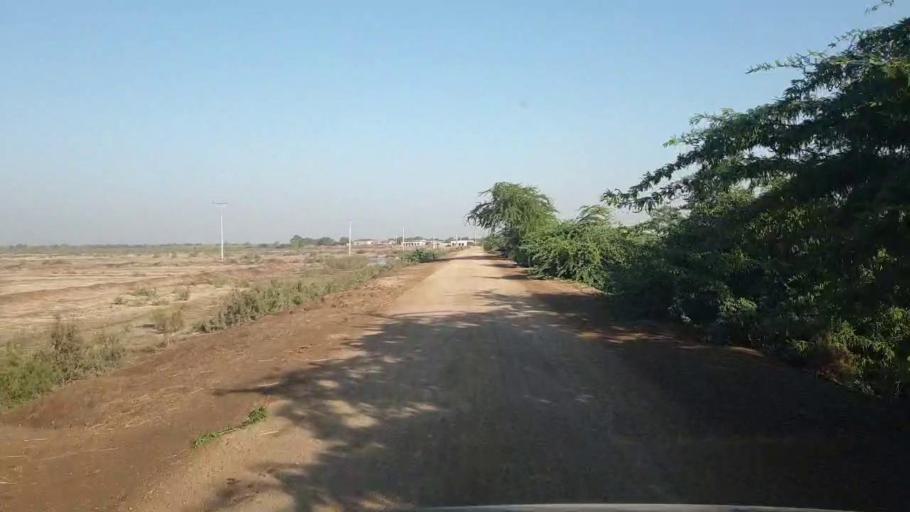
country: PK
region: Sindh
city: Badin
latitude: 24.6976
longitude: 68.8166
